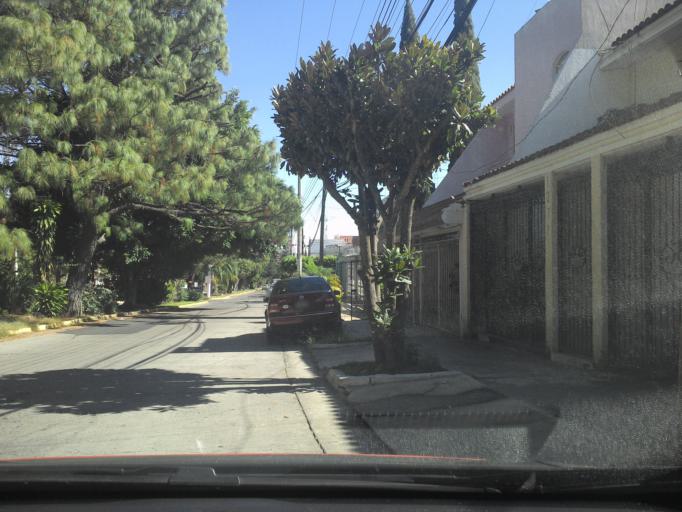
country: MX
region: Jalisco
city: Zapopan2
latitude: 20.7479
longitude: -103.4066
